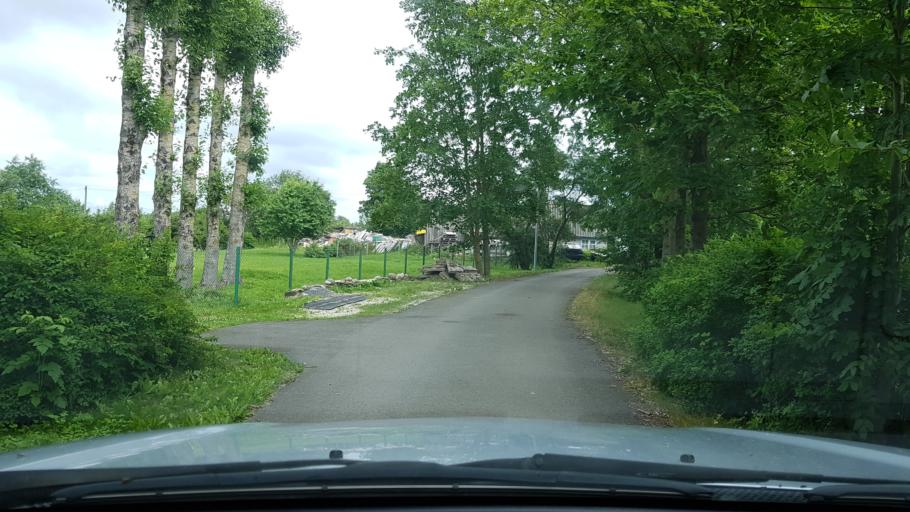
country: EE
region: Ida-Virumaa
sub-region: Narva linn
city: Narva
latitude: 59.3954
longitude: 28.1248
